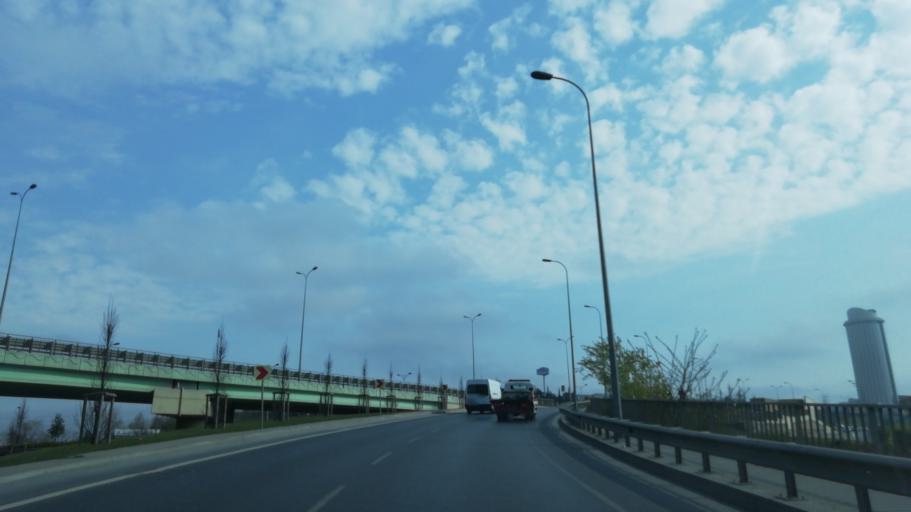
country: TR
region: Istanbul
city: Mahmutbey
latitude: 41.0602
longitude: 28.8145
